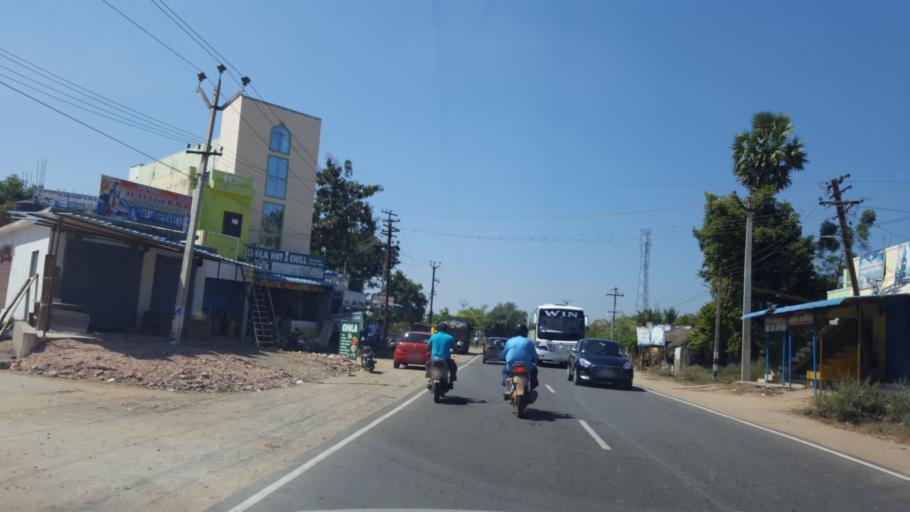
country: IN
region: Tamil Nadu
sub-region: Kancheepuram
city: Chengalpattu
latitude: 12.7065
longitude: 79.9630
